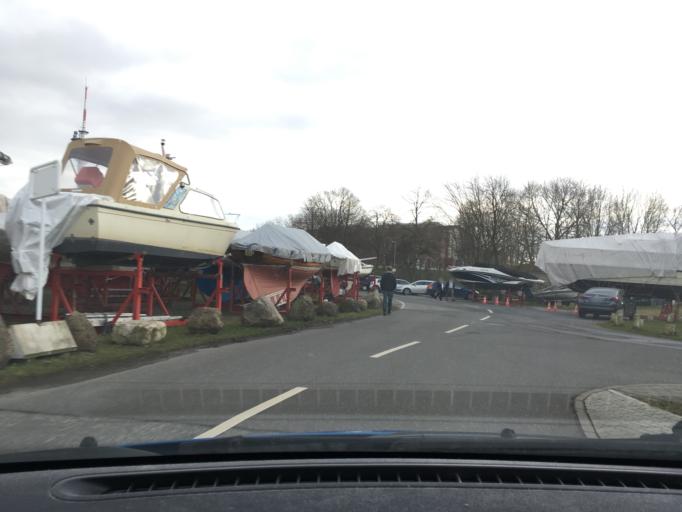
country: DE
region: Schleswig-Holstein
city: Wedel
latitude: 53.5742
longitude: 9.6855
